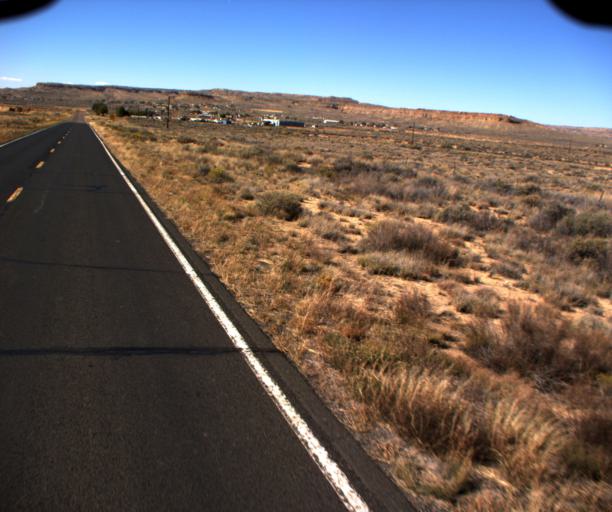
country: US
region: Arizona
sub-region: Navajo County
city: First Mesa
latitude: 35.8732
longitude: -110.5880
